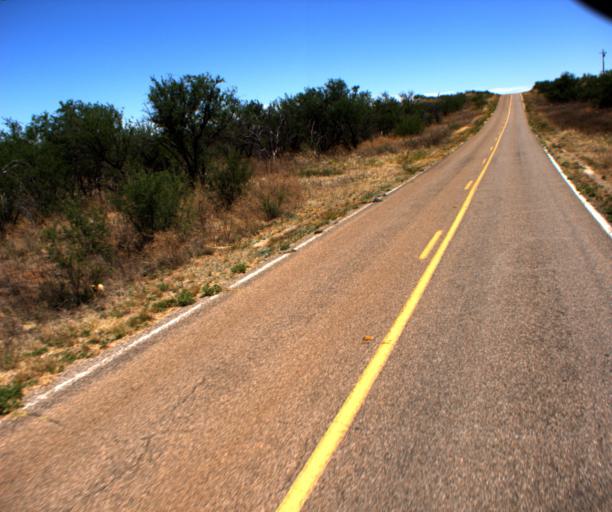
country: US
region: Arizona
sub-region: Santa Cruz County
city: Tubac
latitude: 31.5442
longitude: -111.5402
